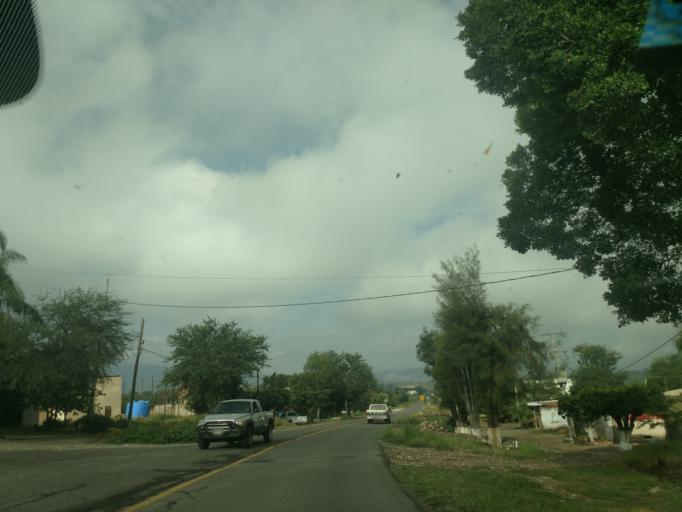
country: MX
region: Jalisco
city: Ameca
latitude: 20.5352
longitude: -104.0525
